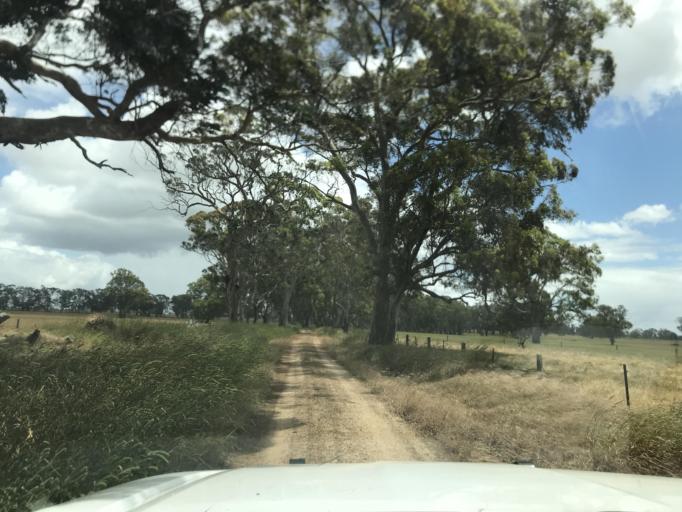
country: AU
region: South Australia
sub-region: Wattle Range
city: Penola
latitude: -37.0882
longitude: 141.3278
